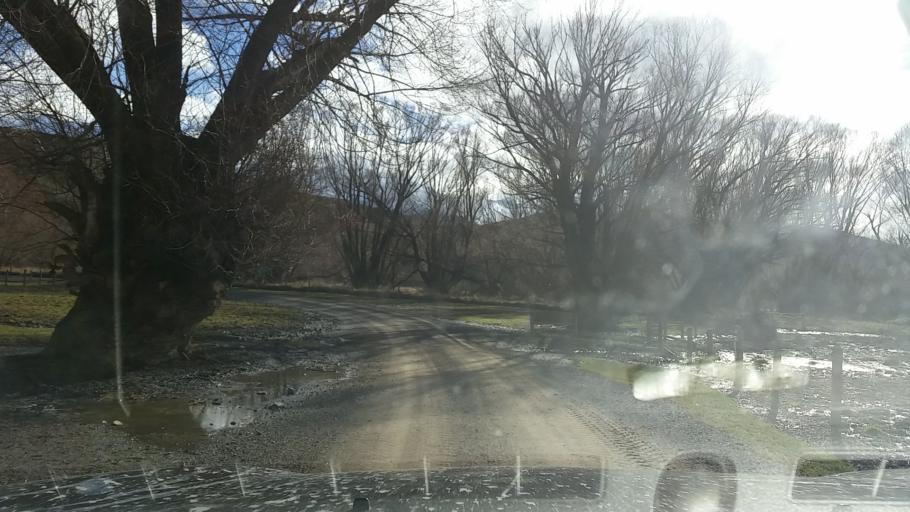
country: NZ
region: Canterbury
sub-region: Kaikoura District
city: Kaikoura
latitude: -42.0461
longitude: 173.3779
